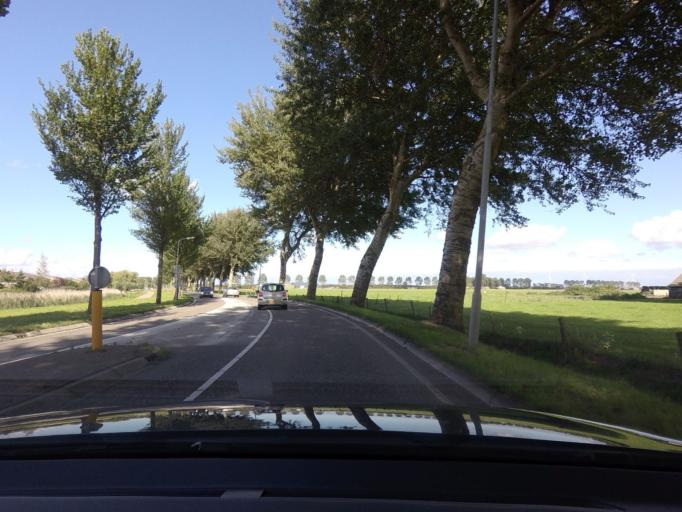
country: NL
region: North Holland
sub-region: Gemeente Schagen
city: Harenkarspel
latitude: 52.7166
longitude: 4.7458
